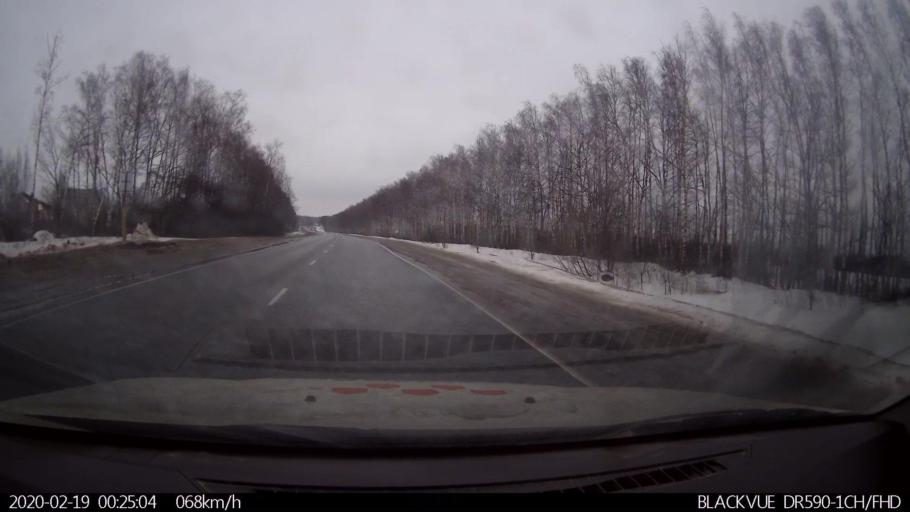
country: RU
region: Nizjnij Novgorod
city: Nizhniy Novgorod
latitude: 56.2185
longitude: 43.9436
